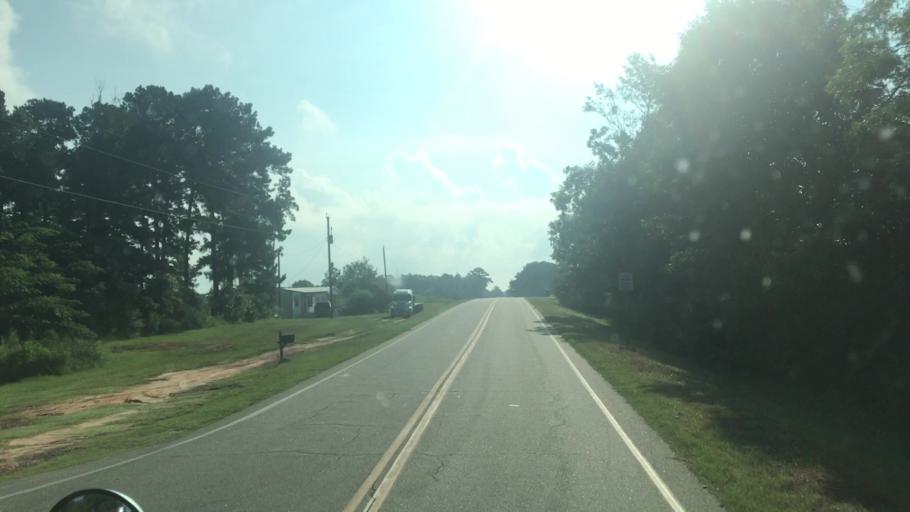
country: US
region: Florida
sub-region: Gadsden County
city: Quincy
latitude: 30.6981
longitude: -84.5342
